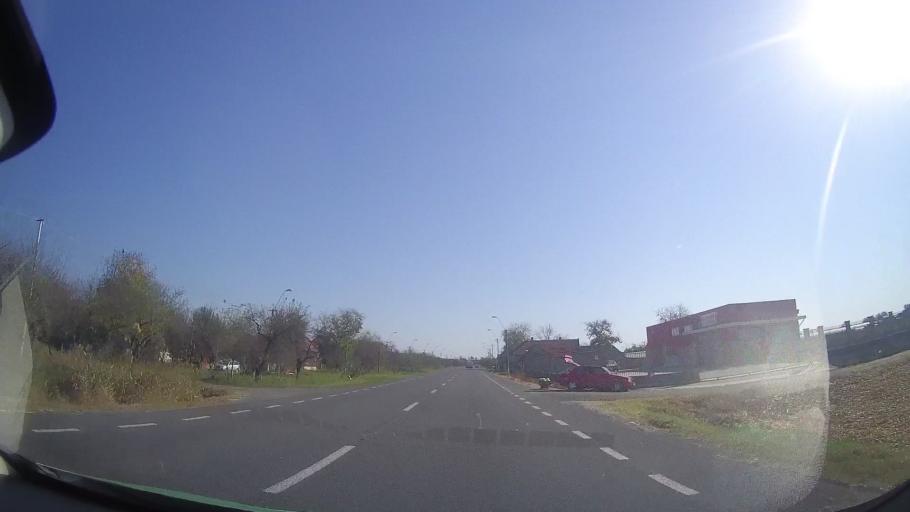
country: RO
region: Timis
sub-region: Comuna Belint
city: Belint
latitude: 45.7541
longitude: 21.7501
